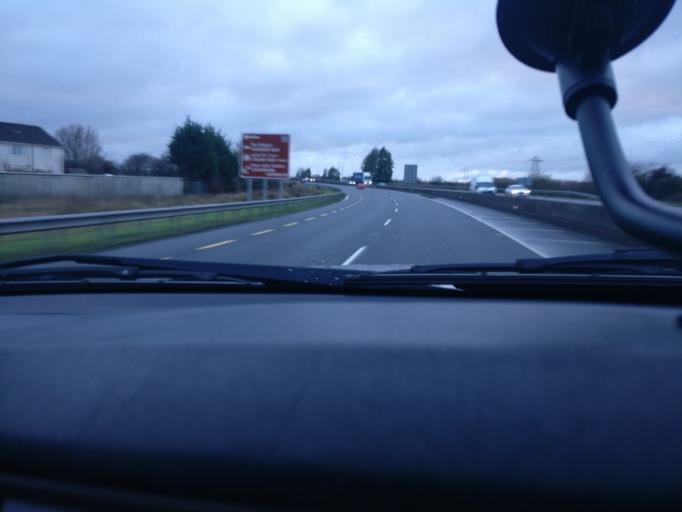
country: IE
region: Leinster
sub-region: An Iarmhi
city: Athlone
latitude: 53.4339
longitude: -7.9503
